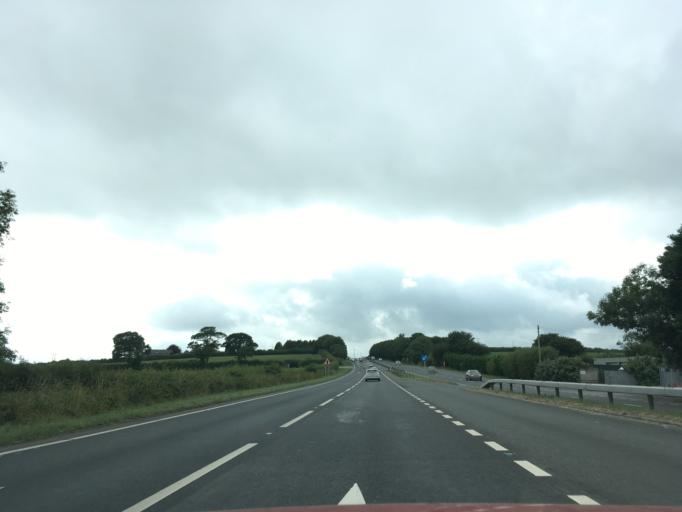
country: GB
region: Wales
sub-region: Carmarthenshire
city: Saint Clears
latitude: 51.8273
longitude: -4.4559
